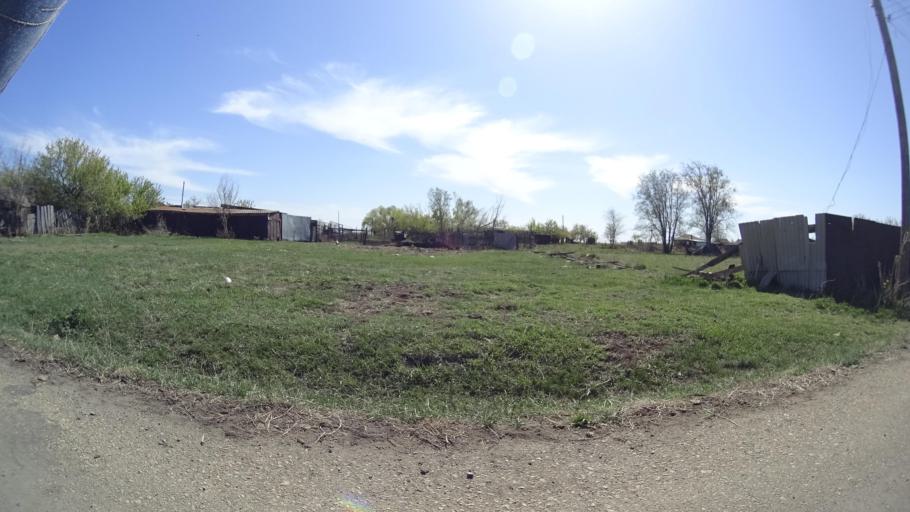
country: RU
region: Chelyabinsk
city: Chesma
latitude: 53.7991
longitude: 61.0193
